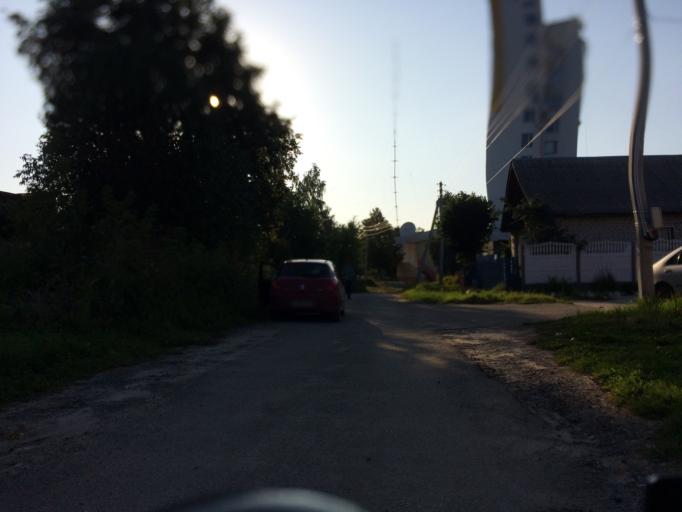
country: RU
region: Mariy-El
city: Yoshkar-Ola
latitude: 56.6210
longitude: 47.8933
